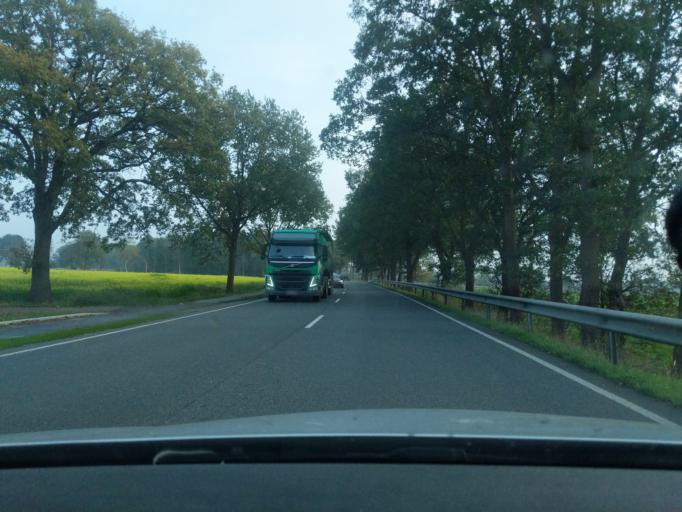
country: DE
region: Lower Saxony
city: Heinbockel
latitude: 53.5977
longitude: 9.3248
